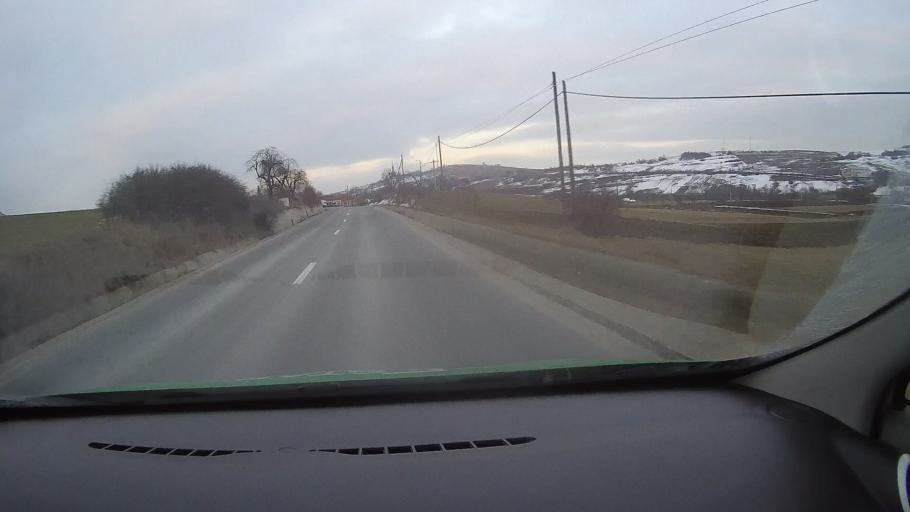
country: RO
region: Harghita
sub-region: Comuna Lupeni
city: Lupeni
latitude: 46.3591
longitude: 25.2351
